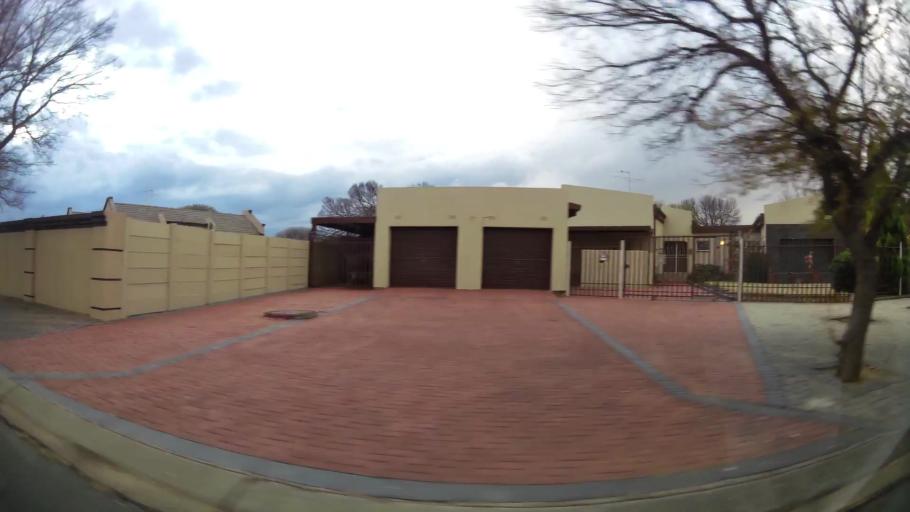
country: ZA
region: Orange Free State
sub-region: Lejweleputswa District Municipality
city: Welkom
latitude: -27.9554
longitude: 26.7398
